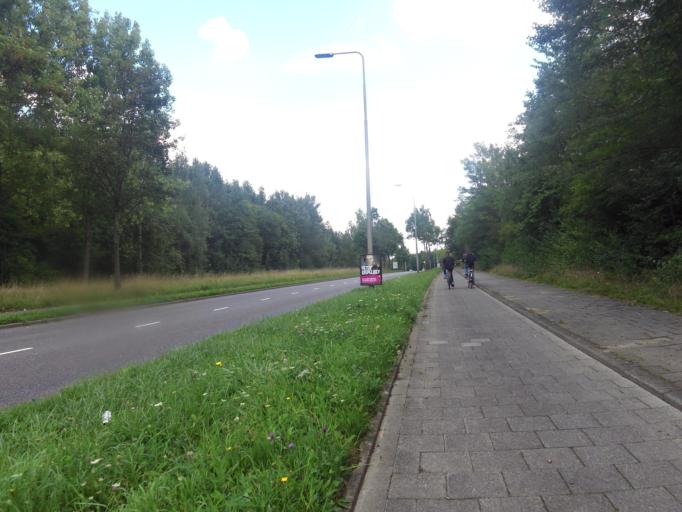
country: NL
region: Limburg
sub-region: Gemeente Heerlen
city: Nieuw-Lotbroek
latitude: 50.9139
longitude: 5.9455
